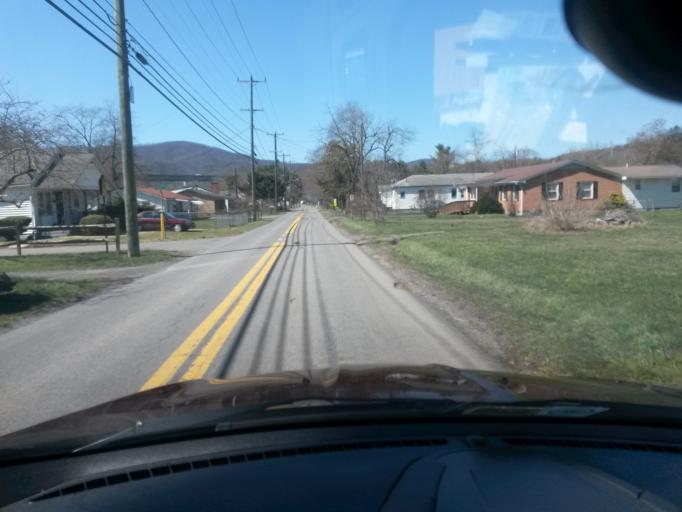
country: US
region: West Virginia
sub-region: Greenbrier County
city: White Sulphur Springs
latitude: 37.7888
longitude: -80.2890
